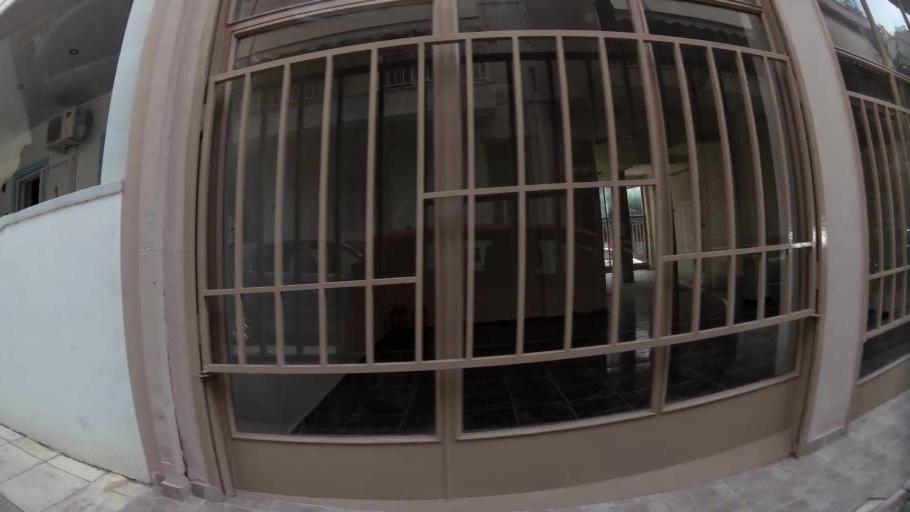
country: GR
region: Attica
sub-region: Nomarchia Athinas
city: Peristeri
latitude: 38.0255
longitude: 23.6803
